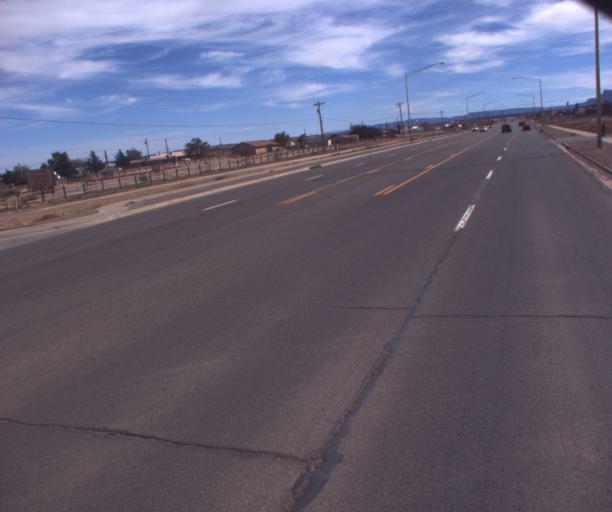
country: US
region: Arizona
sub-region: Navajo County
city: Kayenta
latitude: 36.7127
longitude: -110.2505
